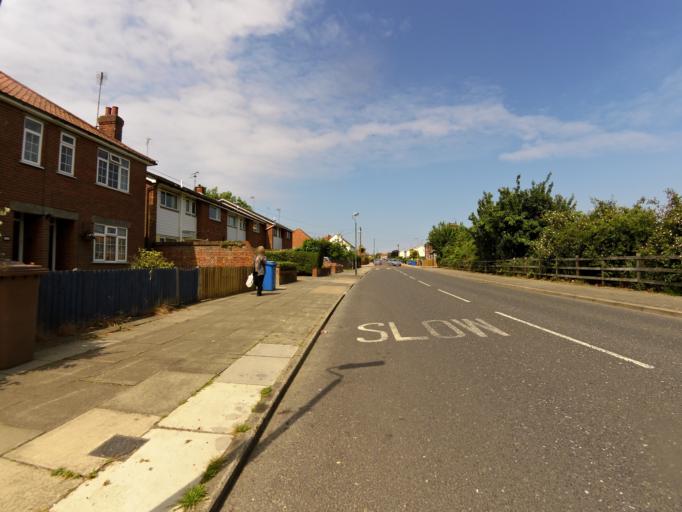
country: GB
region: England
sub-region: Suffolk
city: Bramford
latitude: 52.0712
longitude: 1.1236
